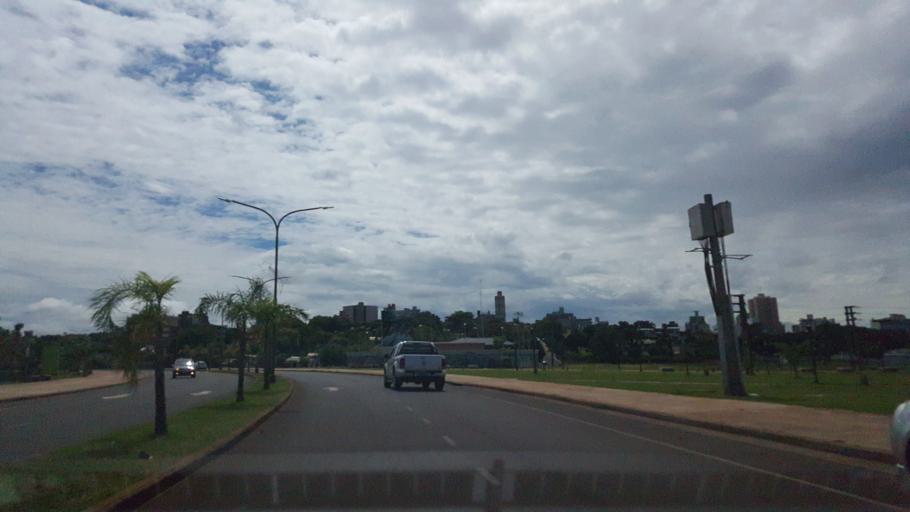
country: AR
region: Misiones
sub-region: Departamento de Capital
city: Posadas
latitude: -27.3565
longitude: -55.9048
